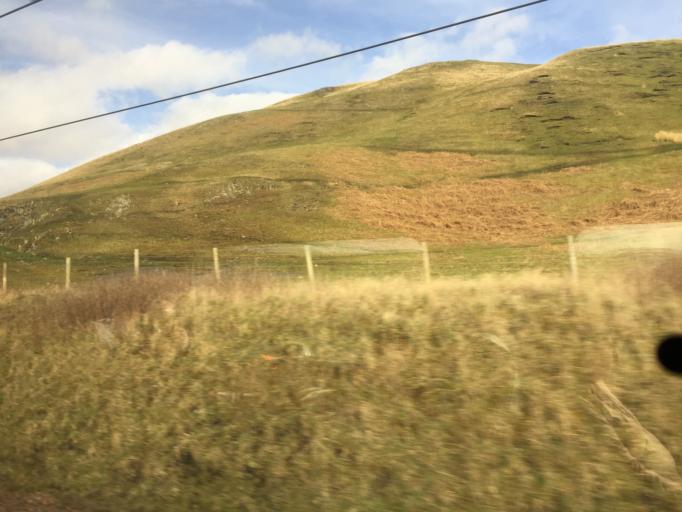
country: GB
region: Scotland
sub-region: South Lanarkshire
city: Douglas
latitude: 55.4746
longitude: -3.6848
